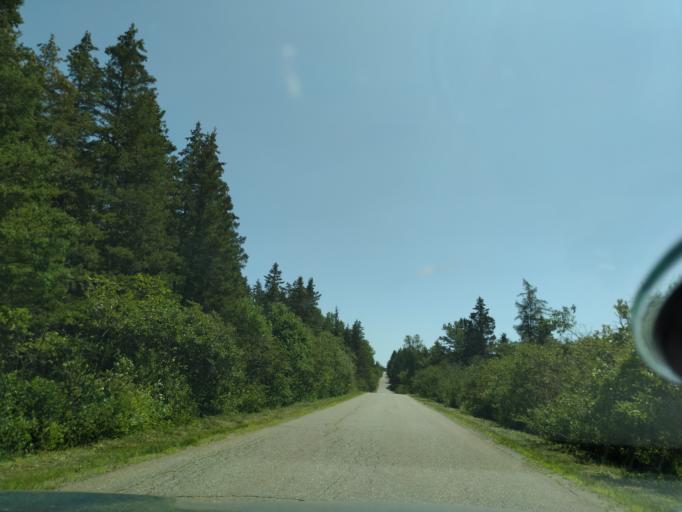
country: US
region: Maine
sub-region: Washington County
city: Eastport
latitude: 44.8365
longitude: -67.0111
